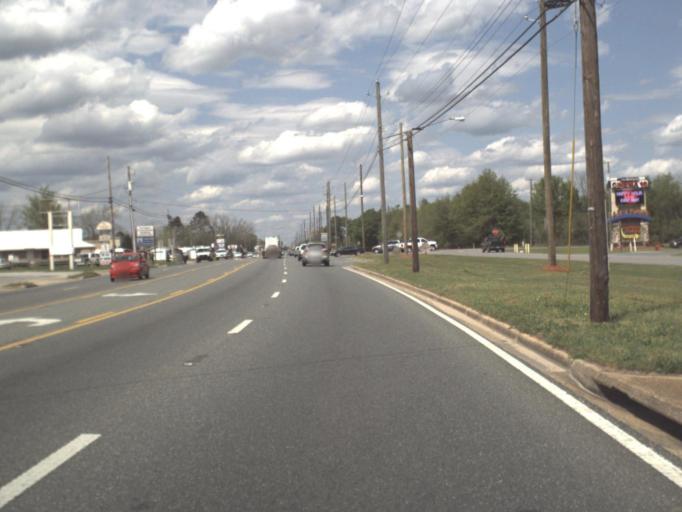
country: US
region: Florida
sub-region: Okaloosa County
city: Crestview
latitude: 30.7791
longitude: -86.5612
